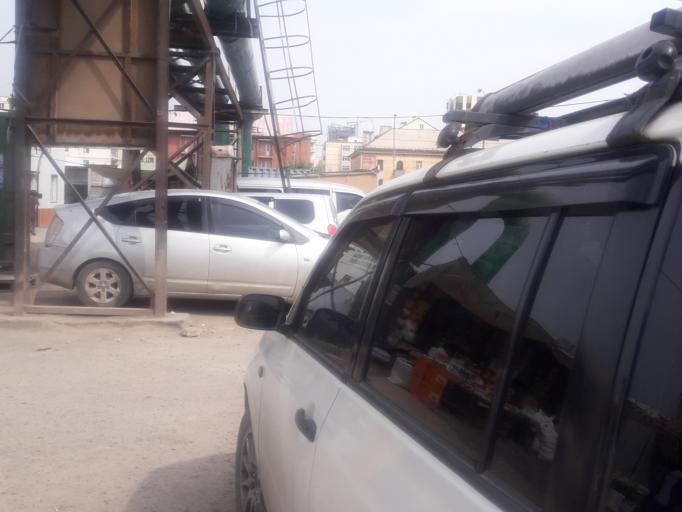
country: MN
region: Ulaanbaatar
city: Ulaanbaatar
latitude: 47.9084
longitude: 106.8929
